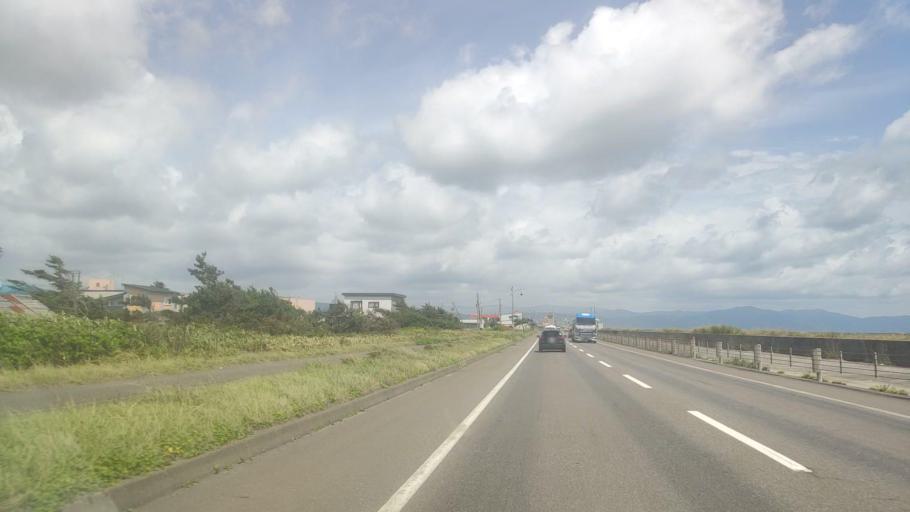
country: JP
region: Hokkaido
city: Niseko Town
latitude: 42.5053
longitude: 140.3733
